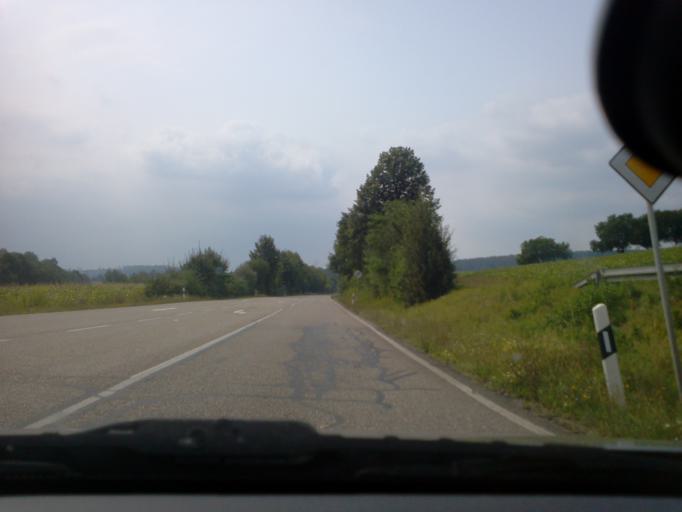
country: DE
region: Baden-Wuerttemberg
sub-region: Karlsruhe Region
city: Woessingen
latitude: 49.0220
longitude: 8.6266
